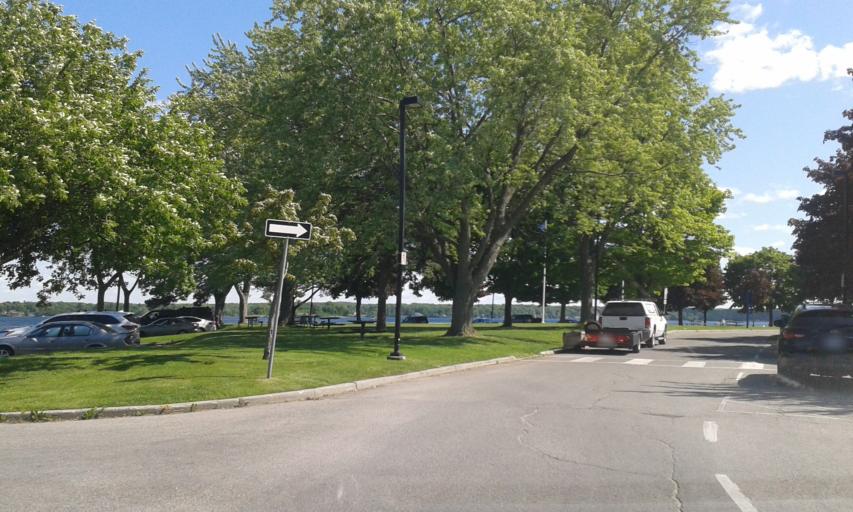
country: CA
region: Ontario
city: Brockville
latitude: 44.5879
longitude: -75.6810
